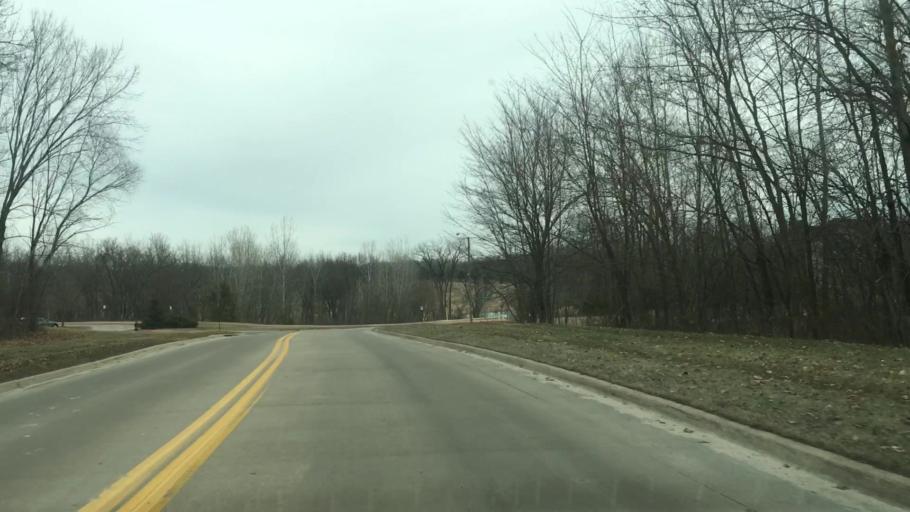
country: US
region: Iowa
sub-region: Johnson County
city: Coralville
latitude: 41.7050
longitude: -91.5764
